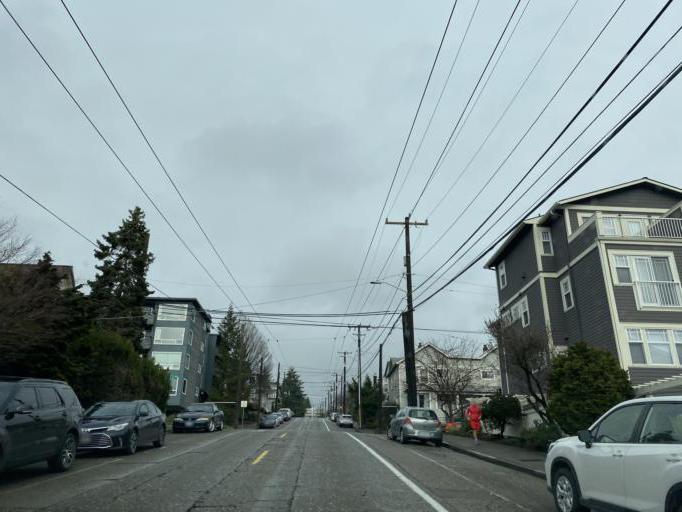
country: US
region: Washington
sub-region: King County
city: Seattle
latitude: 47.6275
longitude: -122.3462
